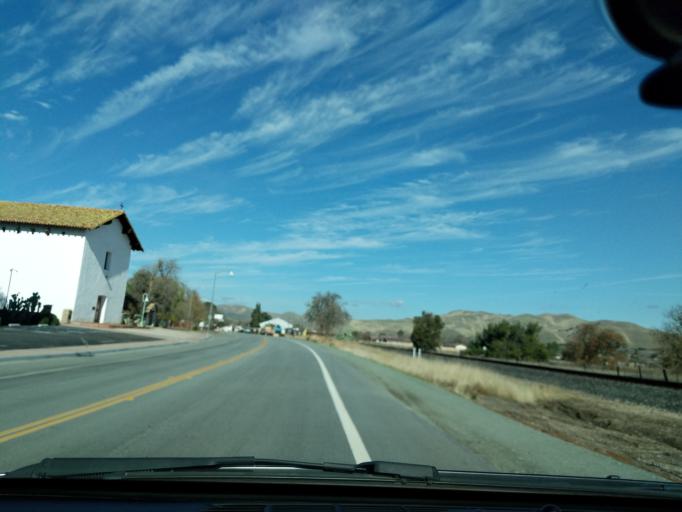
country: US
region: California
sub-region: San Luis Obispo County
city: San Miguel
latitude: 35.7444
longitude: -120.6970
